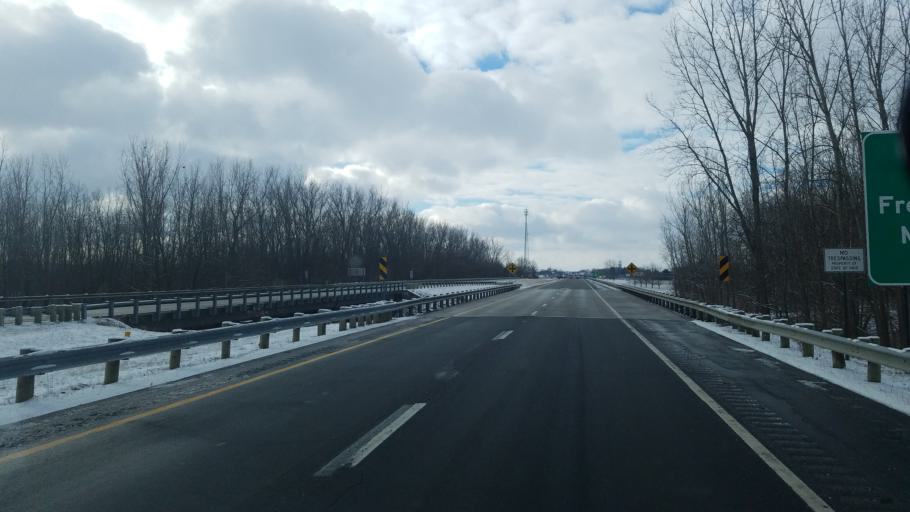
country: US
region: Ohio
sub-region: Knox County
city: Fredericktown
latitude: 40.4958
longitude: -82.5572
